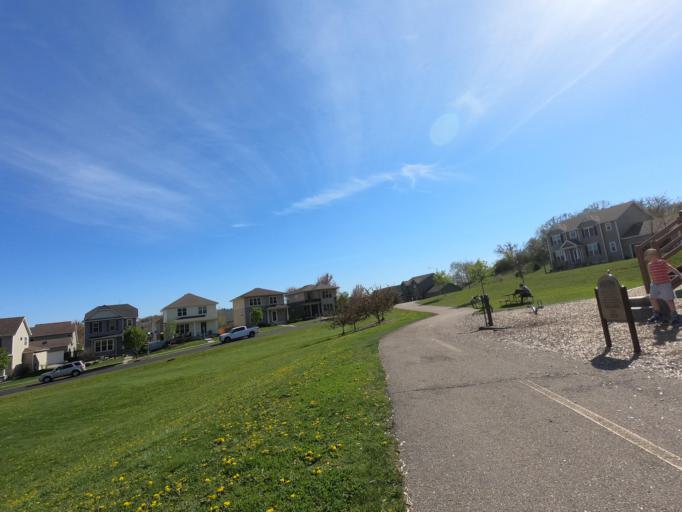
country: US
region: Wisconsin
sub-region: Dane County
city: Middleton
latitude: 43.1035
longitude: -89.5451
